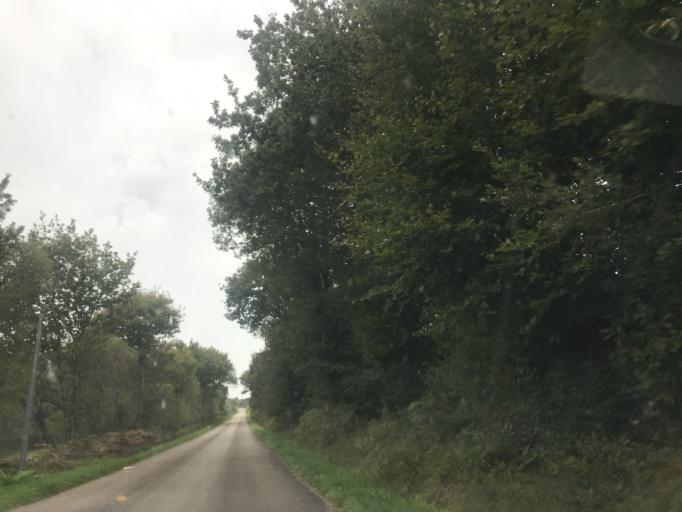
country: FR
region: Brittany
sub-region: Departement du Finistere
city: Plouneour-Menez
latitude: 48.3828
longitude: -3.9336
